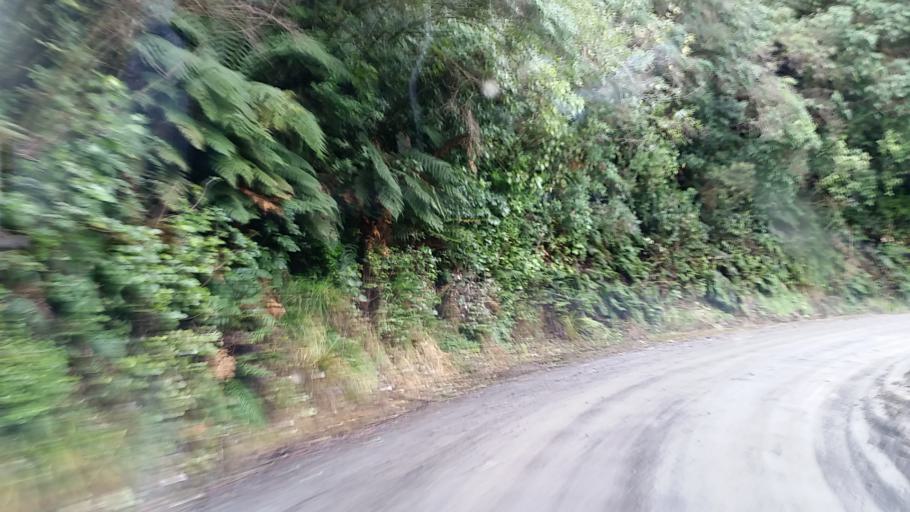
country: NZ
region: Taranaki
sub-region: New Plymouth District
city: Waitara
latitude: -39.1609
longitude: 174.5395
